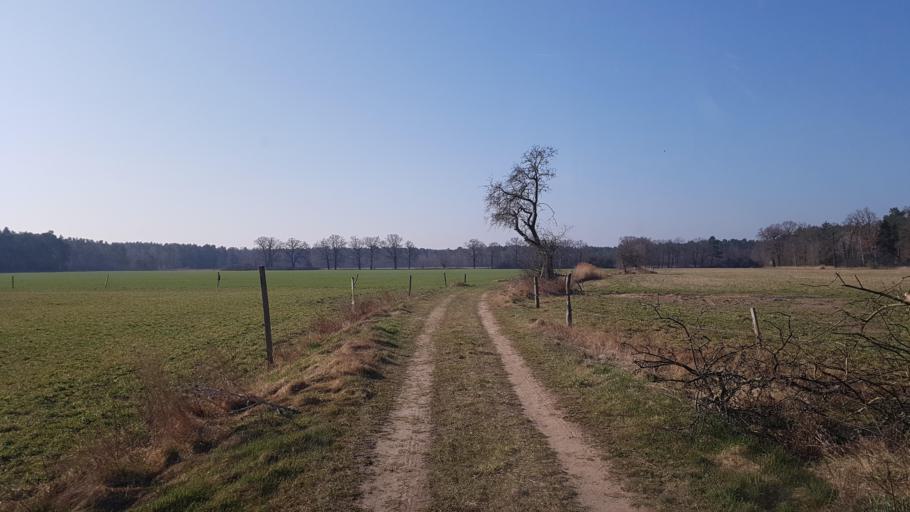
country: DE
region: Brandenburg
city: Altdobern
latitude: 51.7065
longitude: 14.0818
